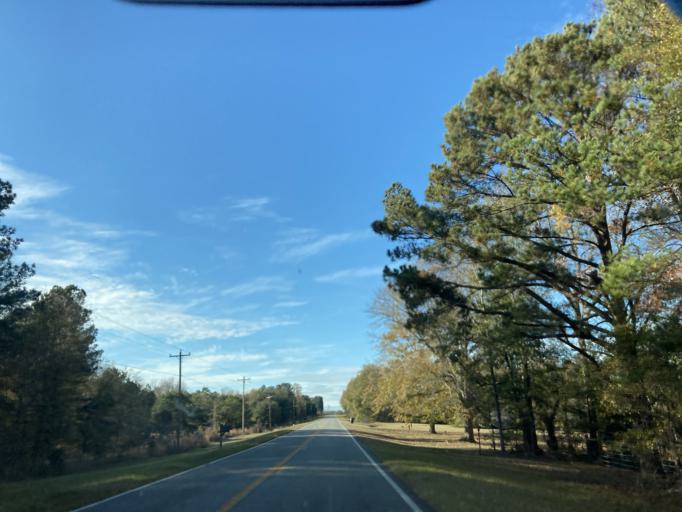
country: US
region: Georgia
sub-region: Jones County
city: Gray
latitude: 32.8910
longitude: -83.5057
